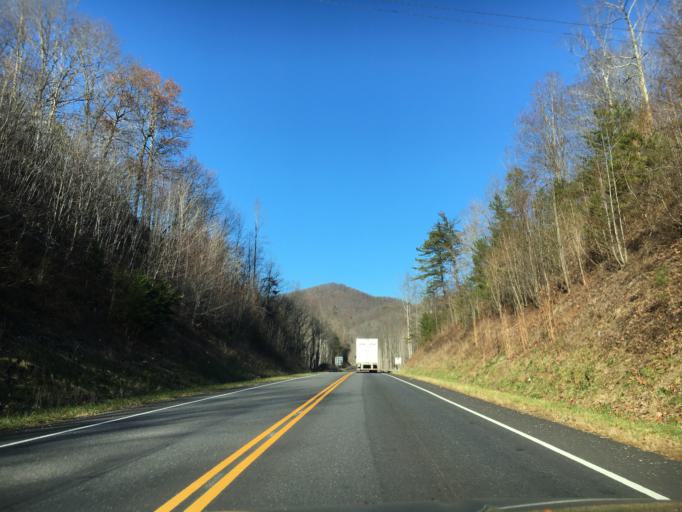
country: US
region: Virginia
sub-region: Patrick County
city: Stuart
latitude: 36.6617
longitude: -80.2755
